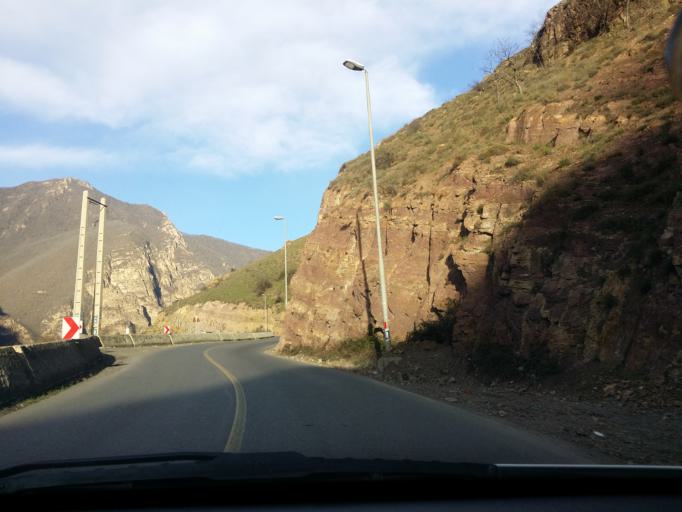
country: IR
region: Mazandaran
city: Chalus
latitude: 36.2651
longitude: 51.2625
